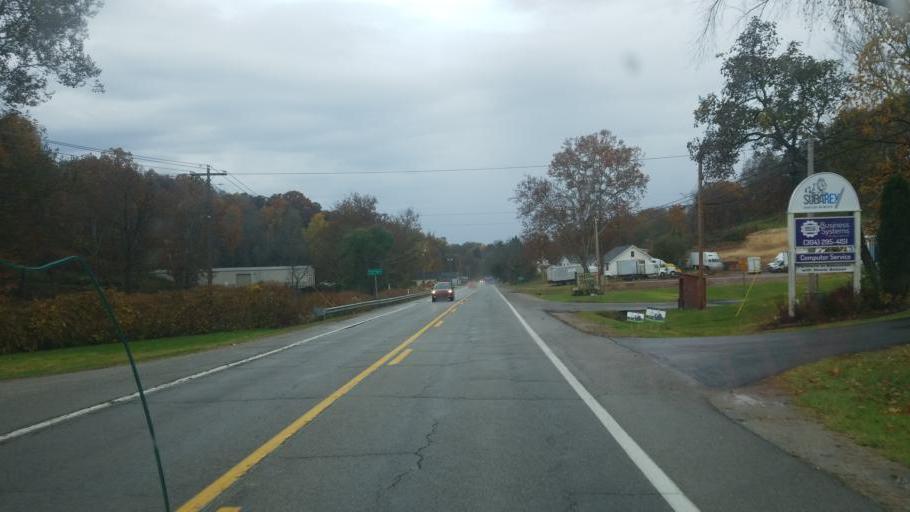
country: US
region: West Virginia
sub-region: Wood County
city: Boaz
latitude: 39.3496
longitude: -81.5154
